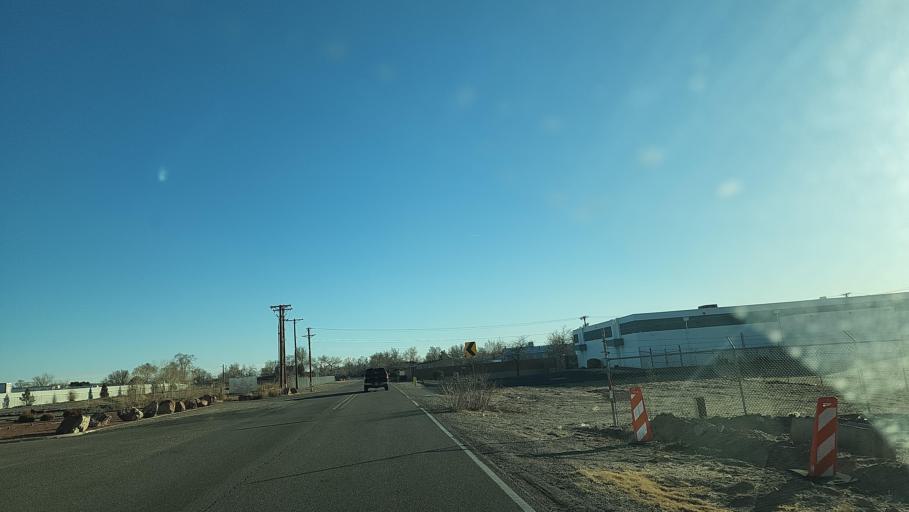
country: US
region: New Mexico
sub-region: Bernalillo County
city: South Valley
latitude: 35.0242
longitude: -106.6542
